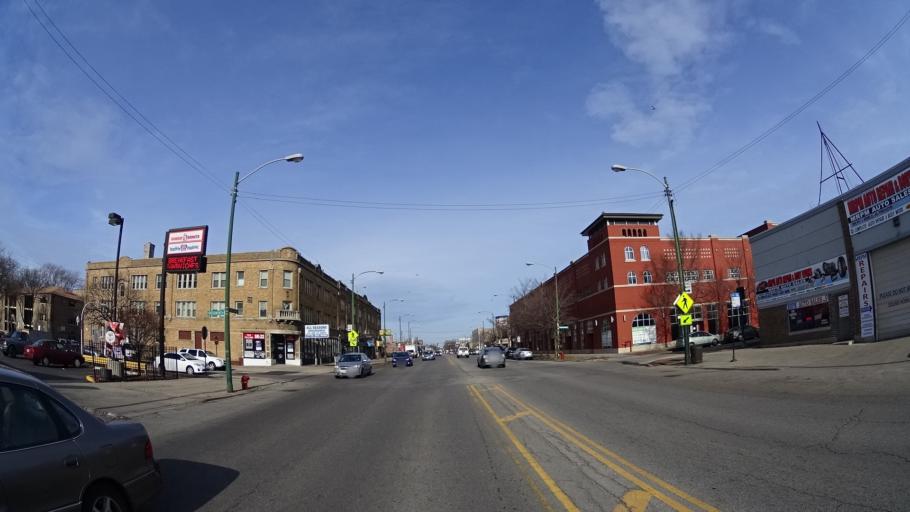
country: US
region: Illinois
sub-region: Cook County
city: Lincolnwood
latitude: 41.9958
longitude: -87.6899
